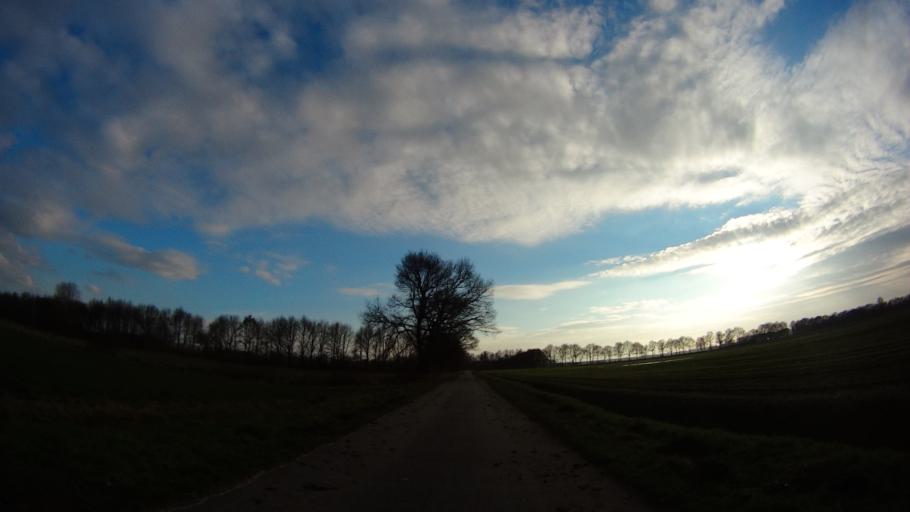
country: NL
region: Drenthe
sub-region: Gemeente Coevorden
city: Sleen
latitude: 52.8169
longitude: 6.7341
